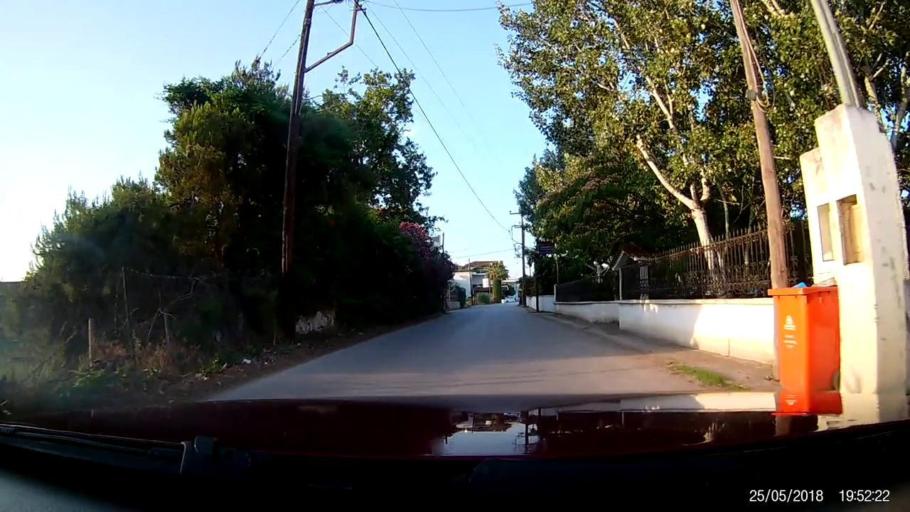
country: GR
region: Central Greece
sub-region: Nomos Evvoias
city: Ayios Nikolaos
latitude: 38.4106
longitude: 23.6449
